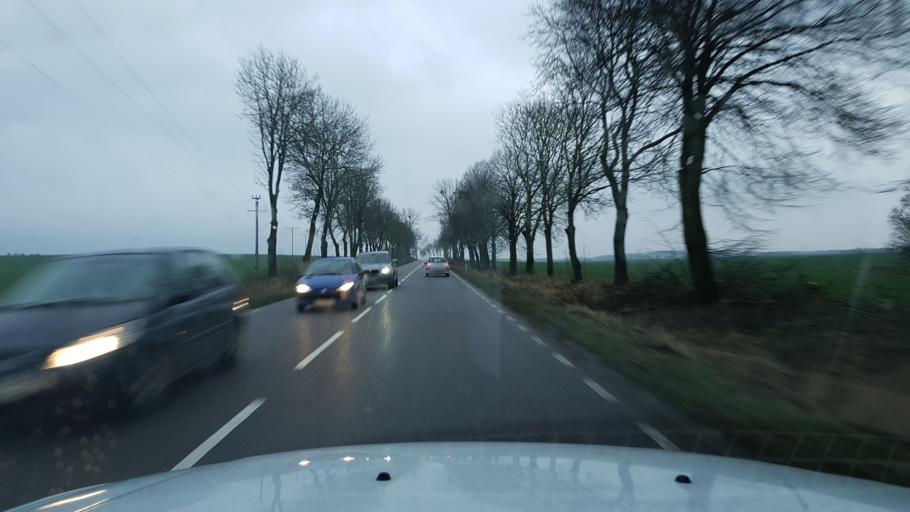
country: PL
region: West Pomeranian Voivodeship
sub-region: Powiat gryficki
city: Ploty
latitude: 53.8541
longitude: 15.2277
